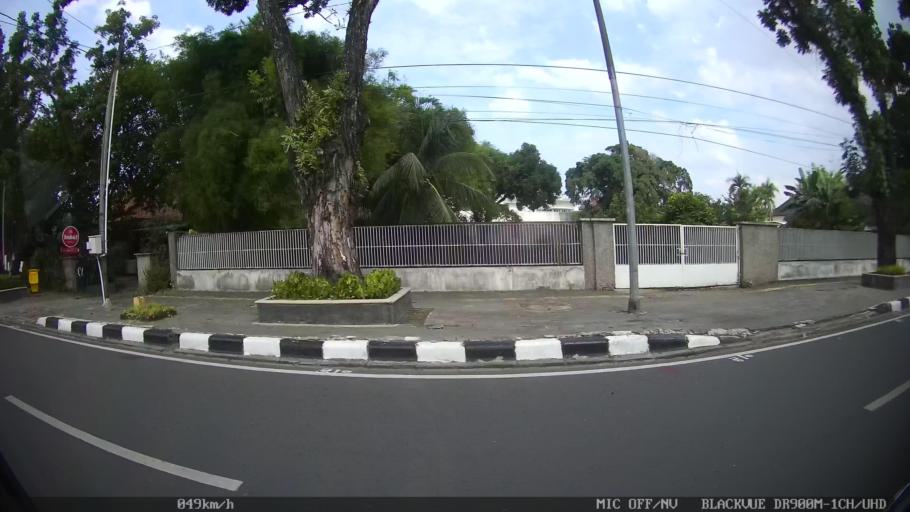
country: ID
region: North Sumatra
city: Medan
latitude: 3.5758
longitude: 98.6722
